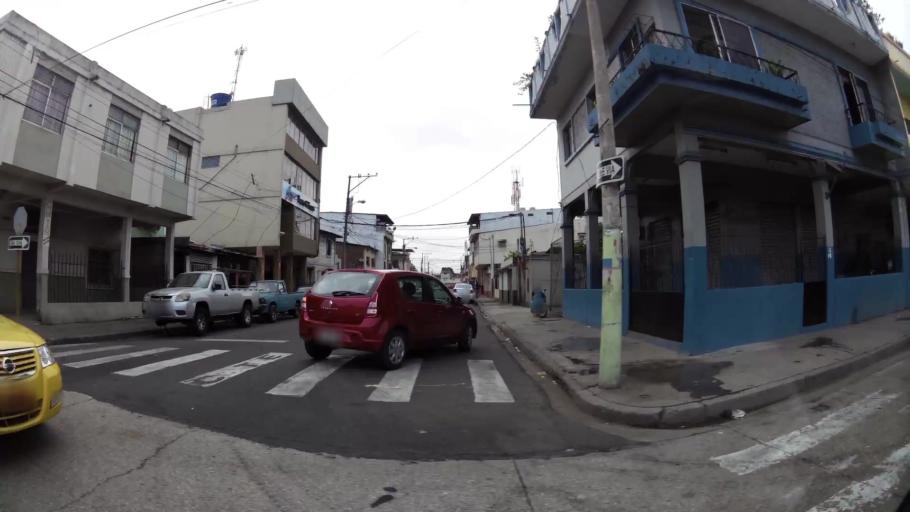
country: EC
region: Guayas
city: Guayaquil
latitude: -2.2158
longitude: -79.8990
